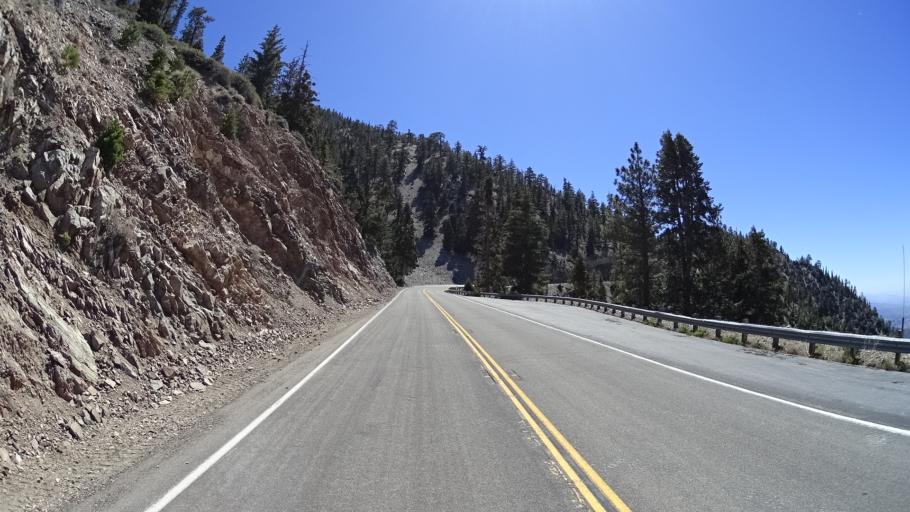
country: US
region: California
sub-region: San Bernardino County
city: Pinon Hills
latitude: 34.3755
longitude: -117.7716
